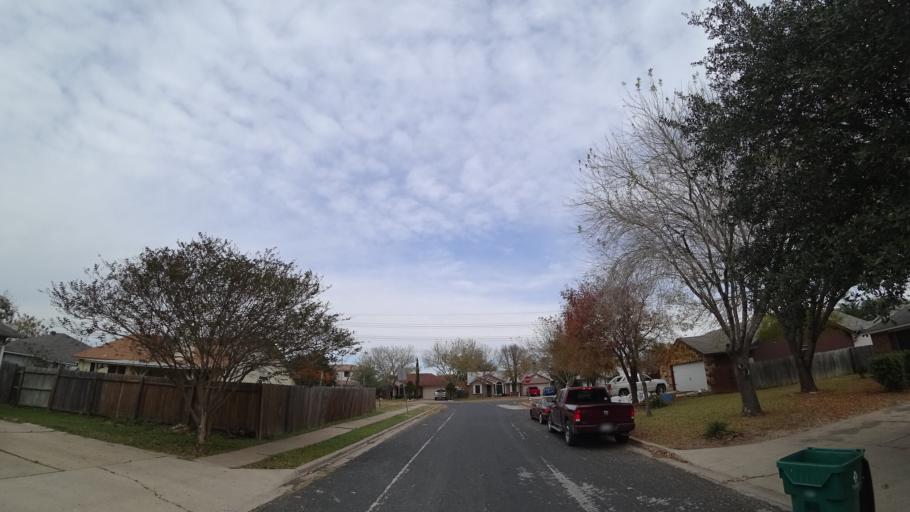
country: US
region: Texas
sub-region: Travis County
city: Garfield
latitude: 30.1586
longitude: -97.6483
